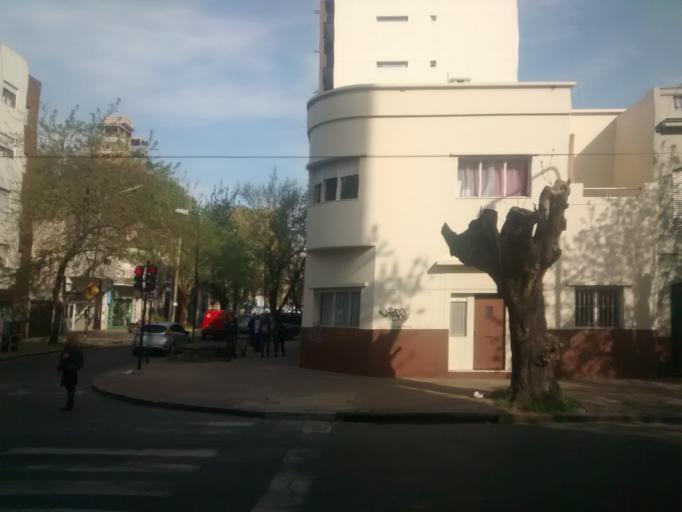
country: AR
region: Buenos Aires
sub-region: Partido de La Plata
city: La Plata
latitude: -34.9218
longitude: -57.9426
